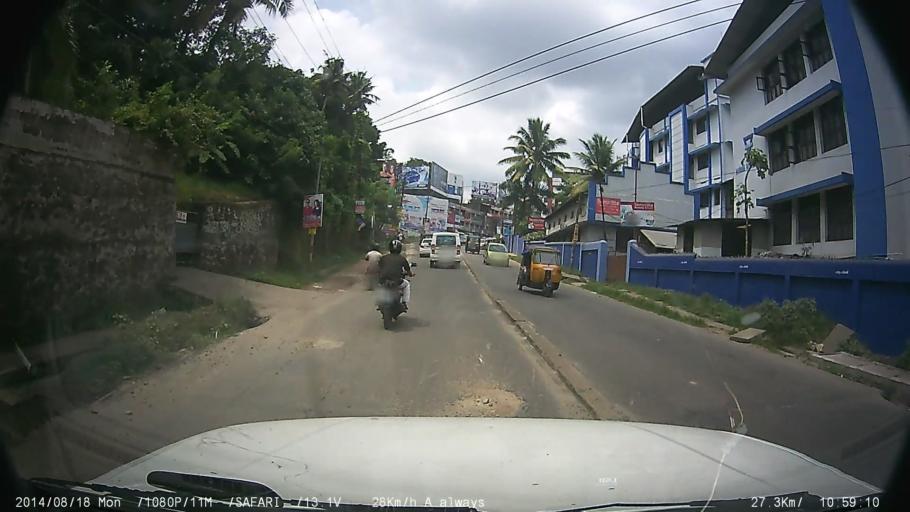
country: IN
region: Kerala
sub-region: Kottayam
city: Kottayam
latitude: 9.5955
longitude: 76.5231
